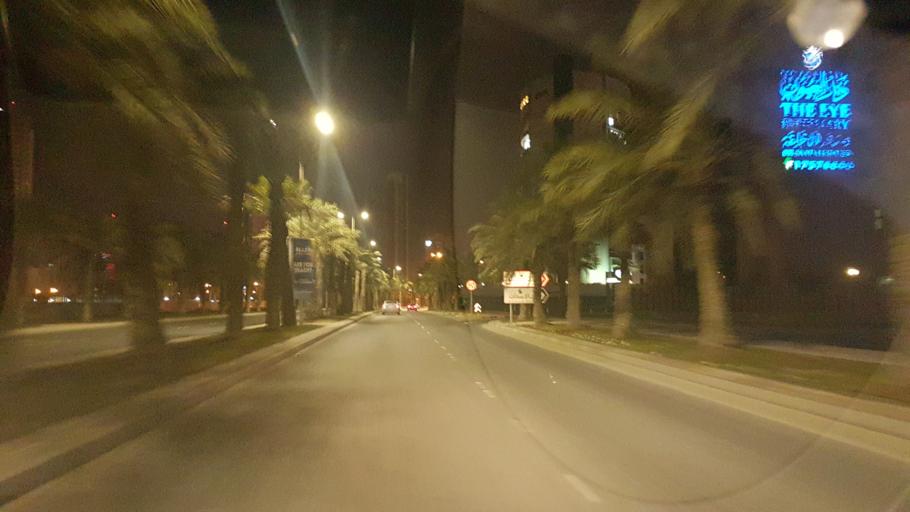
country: BH
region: Manama
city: Jidd Hafs
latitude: 26.2378
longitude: 50.5429
